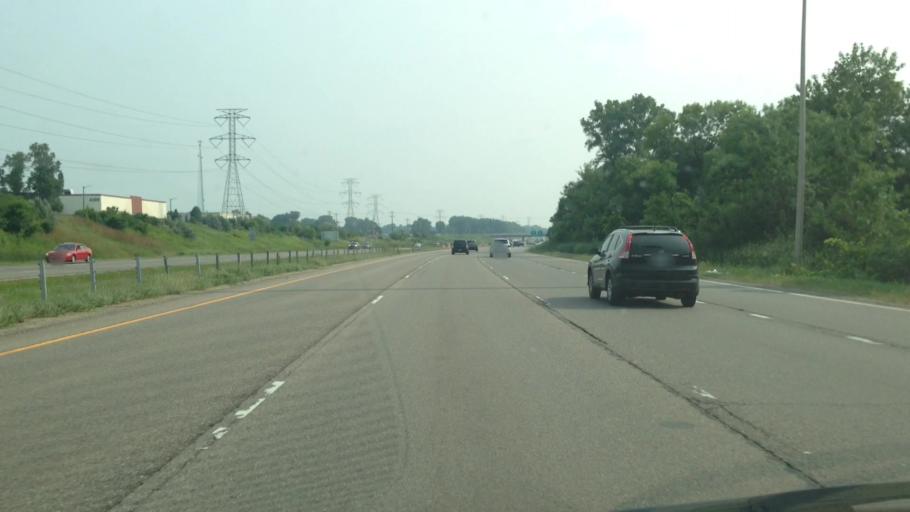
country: US
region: Minnesota
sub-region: Ramsey County
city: New Brighton
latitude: 45.0755
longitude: -93.1855
